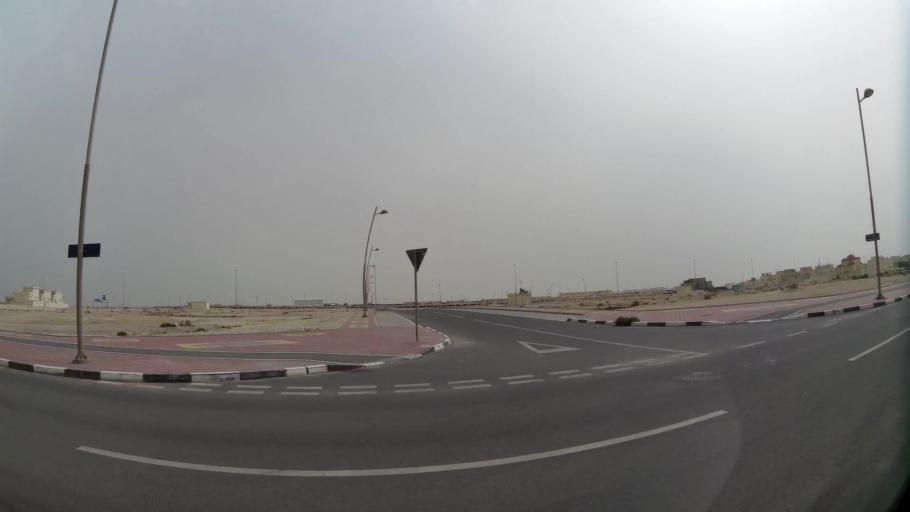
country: QA
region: Baladiyat ad Dawhah
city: Doha
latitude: 25.2279
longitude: 51.5483
